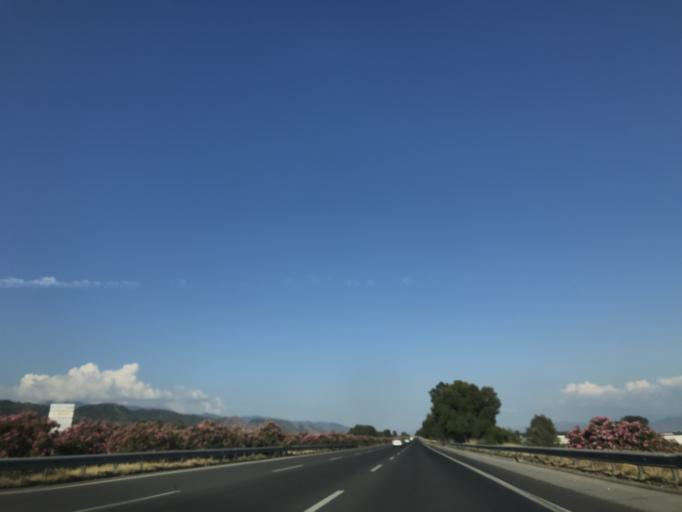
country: TR
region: Aydin
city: Germencik
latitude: 37.8702
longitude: 27.6398
